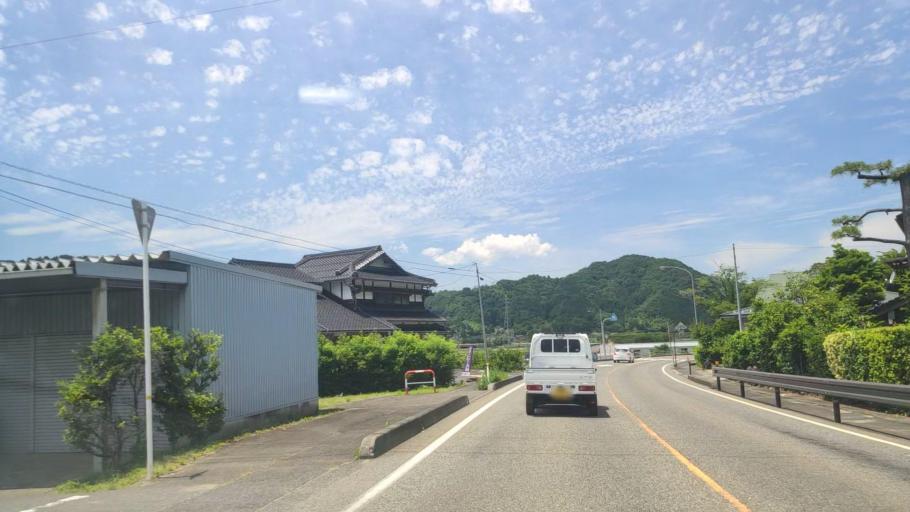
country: JP
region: Tottori
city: Tottori
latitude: 35.3755
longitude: 134.3009
